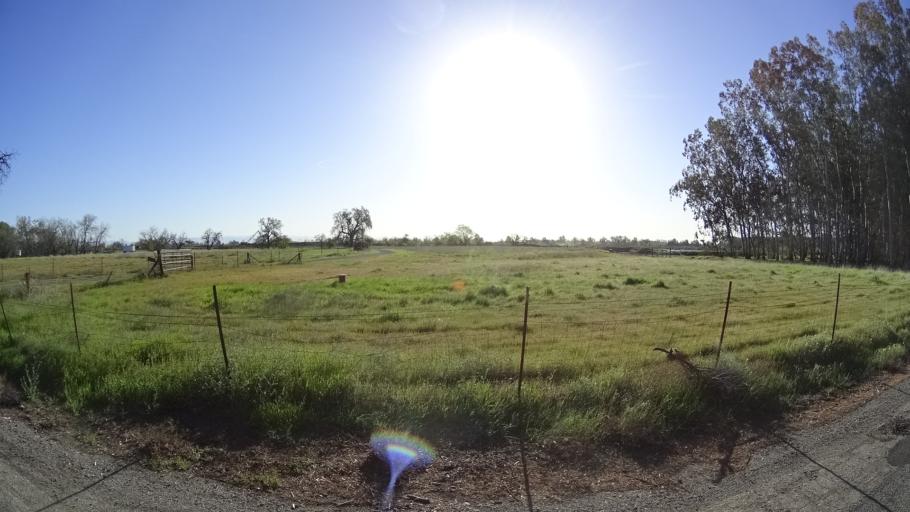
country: US
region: California
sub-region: Glenn County
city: Orland
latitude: 39.7690
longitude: -122.2154
